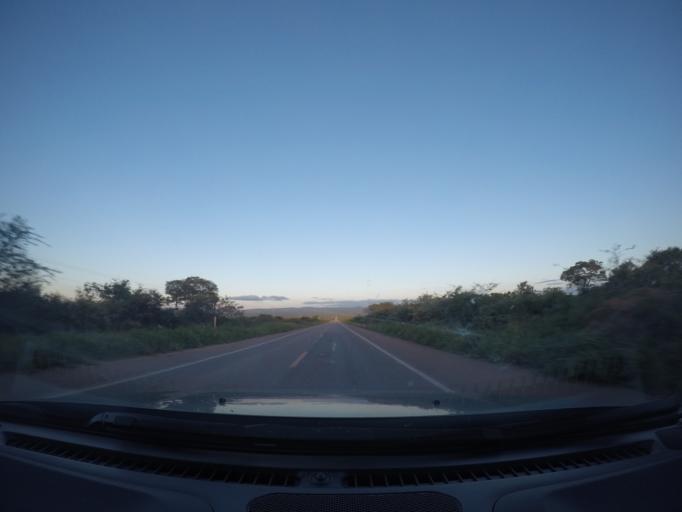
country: BR
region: Bahia
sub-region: Seabra
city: Seabra
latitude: -12.4095
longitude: -41.9670
